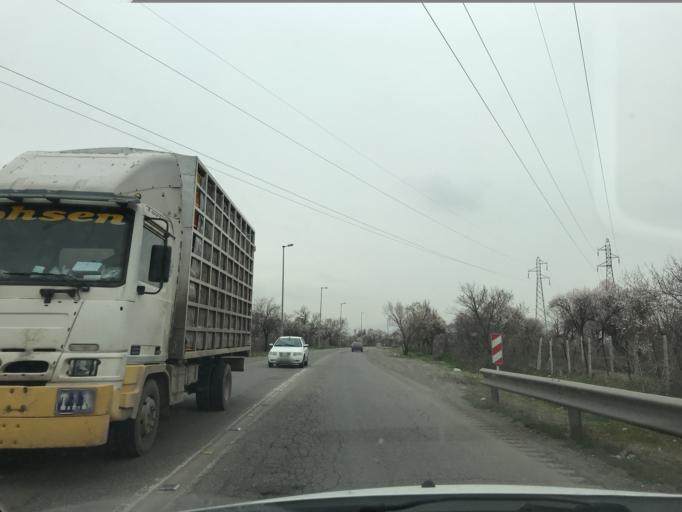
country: IR
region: Qazvin
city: Qazvin
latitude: 36.2766
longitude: 49.9786
